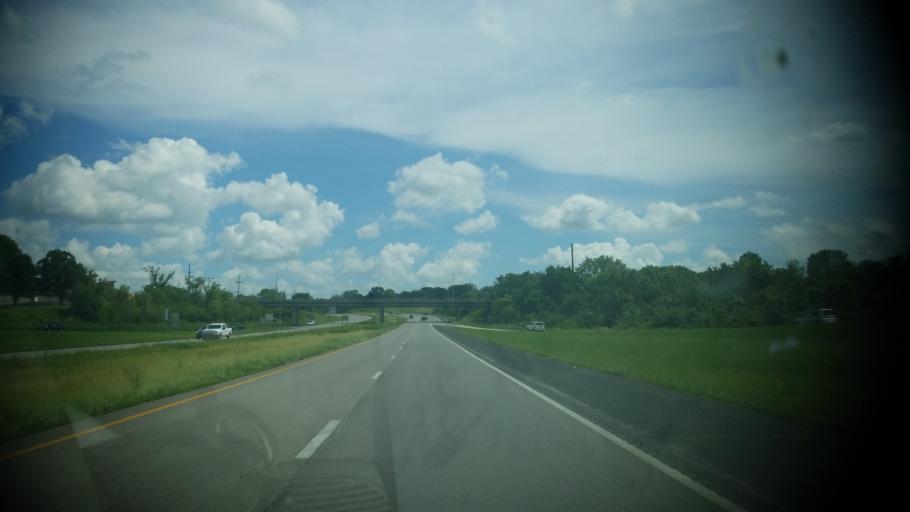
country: US
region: Missouri
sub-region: Lincoln County
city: Troy
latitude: 38.9861
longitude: -90.9656
